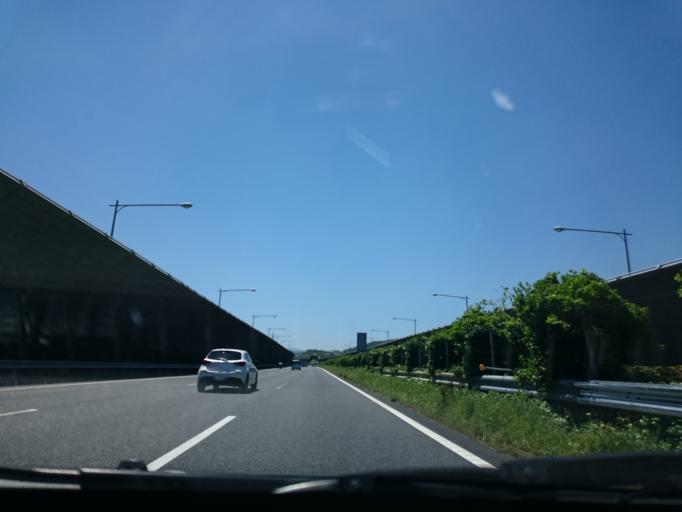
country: JP
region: Kanagawa
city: Isehara
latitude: 35.3844
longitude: 139.2743
